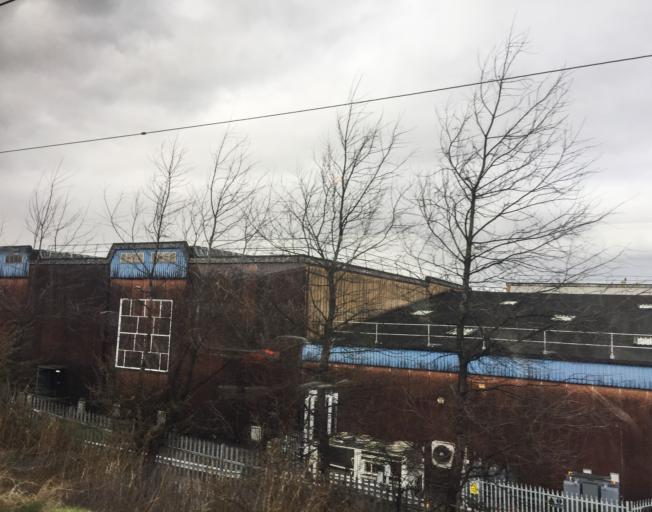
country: GB
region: Scotland
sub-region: West Dunbartonshire
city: Clydebank
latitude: 55.9056
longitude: -4.3727
